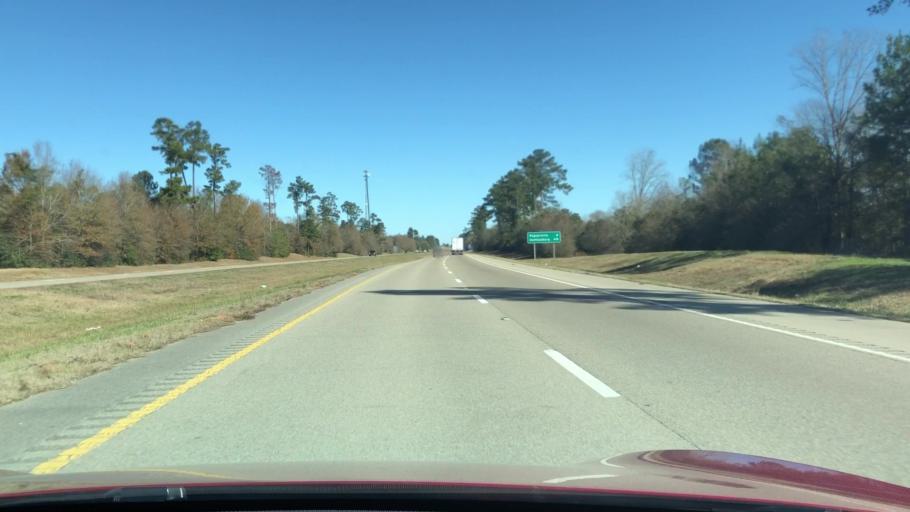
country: US
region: Mississippi
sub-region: Pearl River County
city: Poplarville
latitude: 30.7282
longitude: -89.5484
